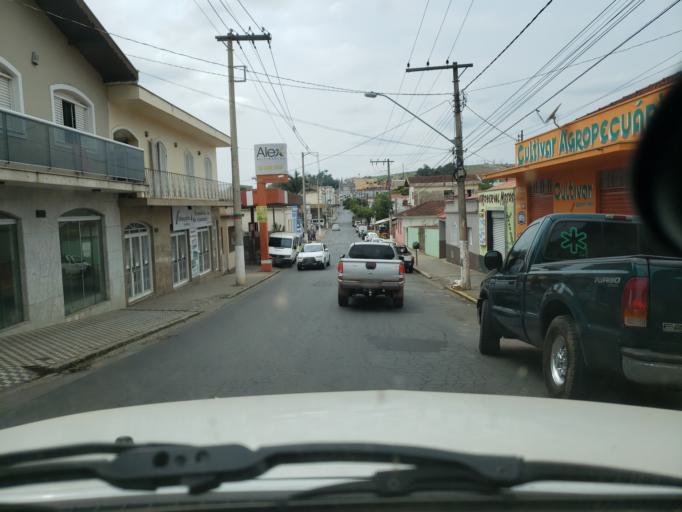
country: BR
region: Minas Gerais
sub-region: Jacutinga
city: Jacutinga
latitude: -22.2830
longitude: -46.6117
